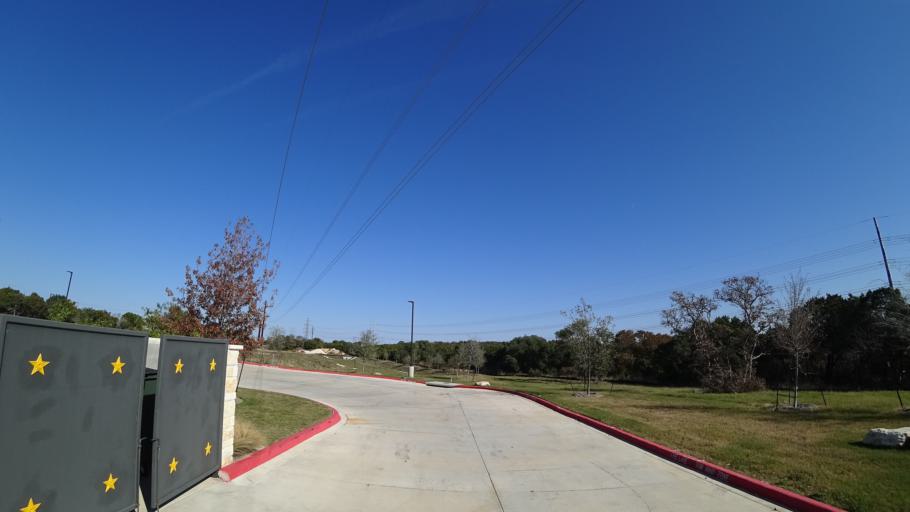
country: US
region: Texas
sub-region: Travis County
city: Hudson Bend
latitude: 30.3938
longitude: -97.8660
